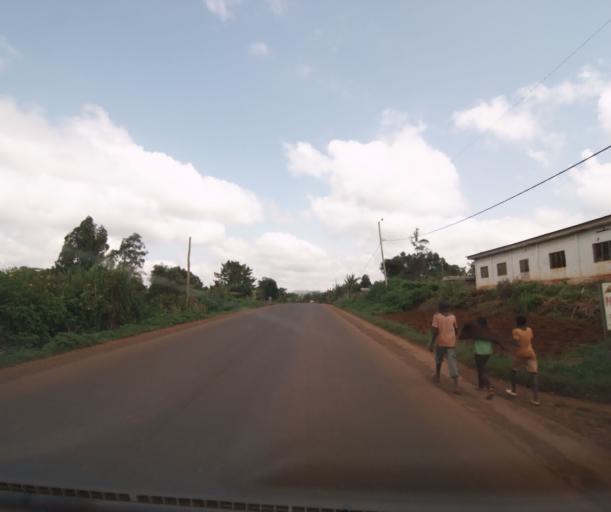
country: CM
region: West
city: Dschang
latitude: 5.4955
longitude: 10.1600
